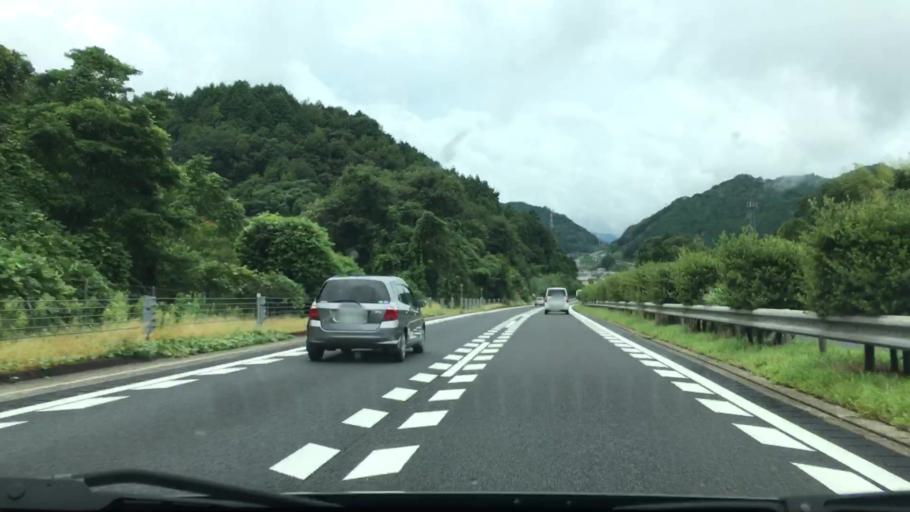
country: JP
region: Hyogo
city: Yamazakicho-nakabirose
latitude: 34.9758
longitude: 134.6406
